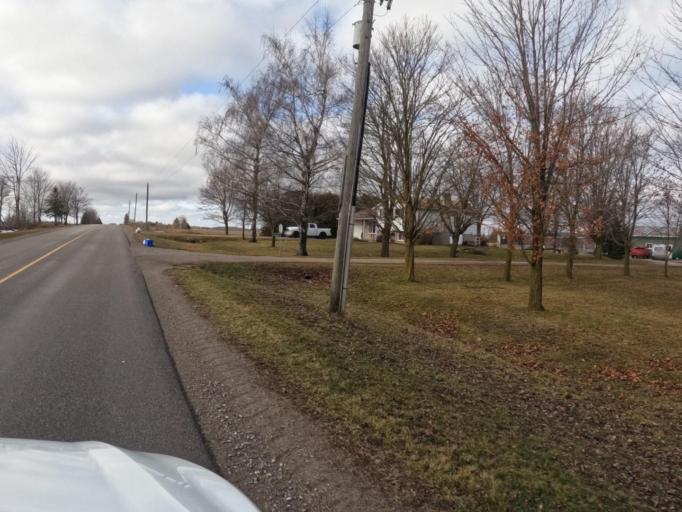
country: CA
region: Ontario
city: Shelburne
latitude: 43.8913
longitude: -80.3526
